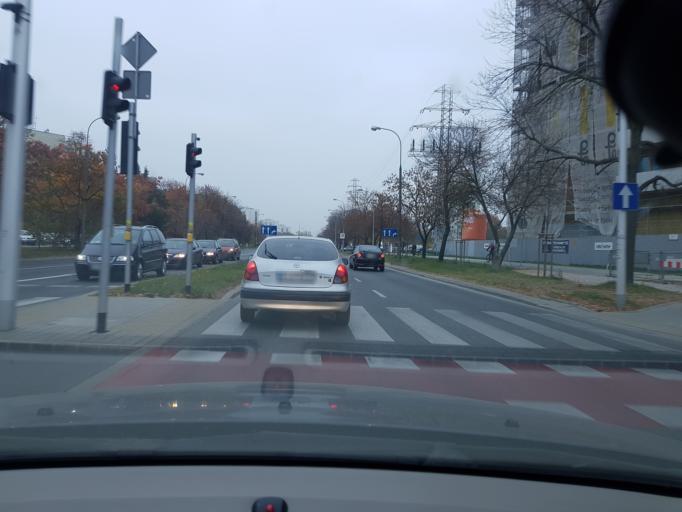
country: PL
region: Masovian Voivodeship
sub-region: Warszawa
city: Ursynow
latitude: 52.1511
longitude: 21.0352
